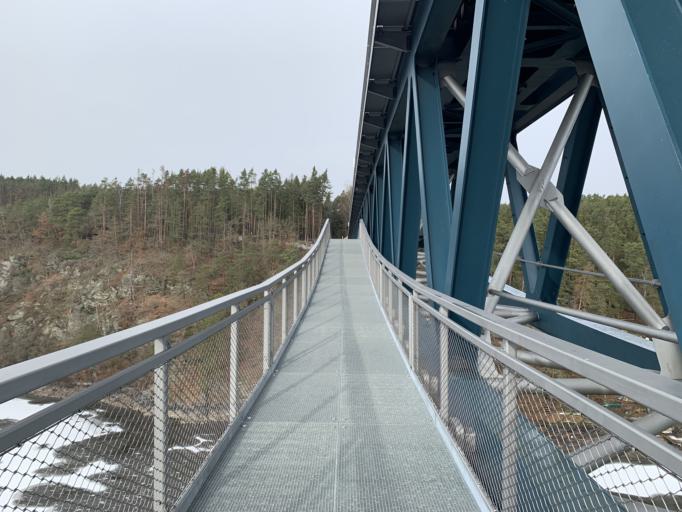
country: CZ
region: Plzensky
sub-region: Okres Tachov
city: Stribro
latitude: 49.7859
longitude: 13.0743
